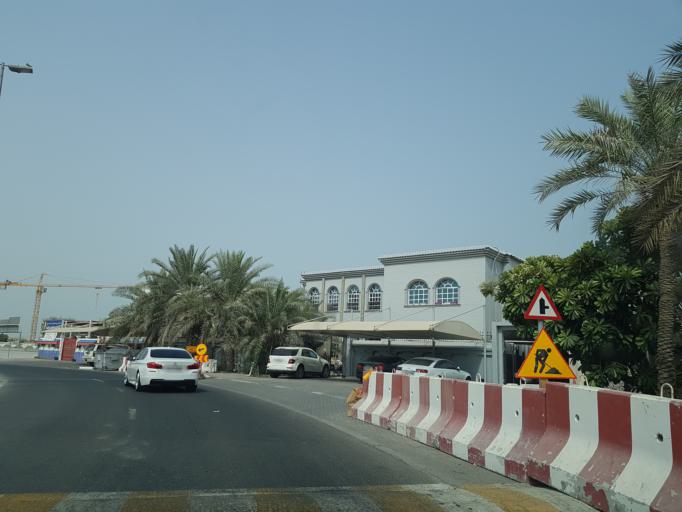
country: AE
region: Ash Shariqah
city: Sharjah
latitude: 25.2447
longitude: 55.2899
